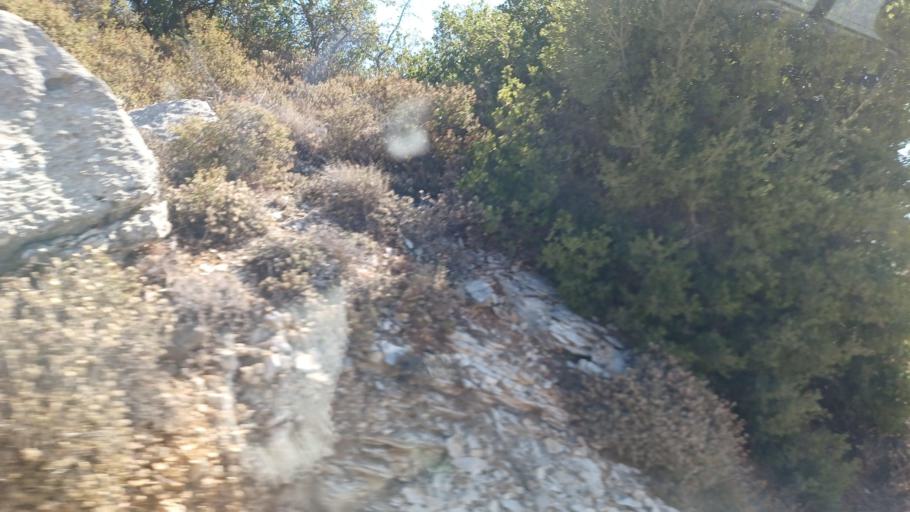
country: CY
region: Limassol
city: Pachna
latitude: 34.8985
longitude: 32.6384
